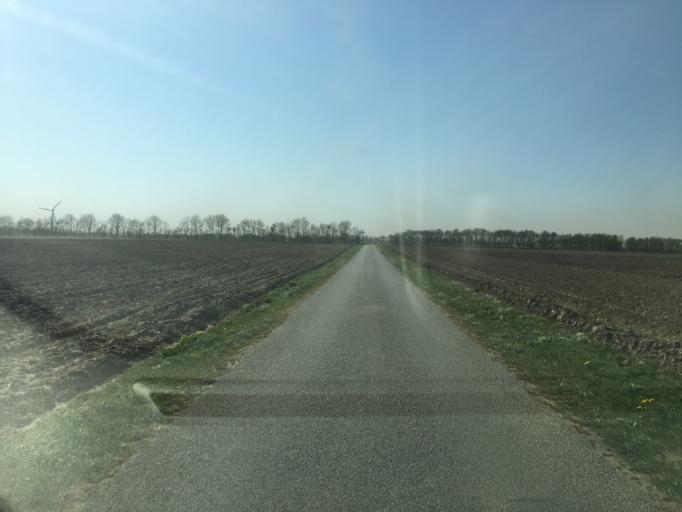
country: DK
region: South Denmark
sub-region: Aabenraa Kommune
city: Rodekro
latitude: 55.1128
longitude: 9.1911
